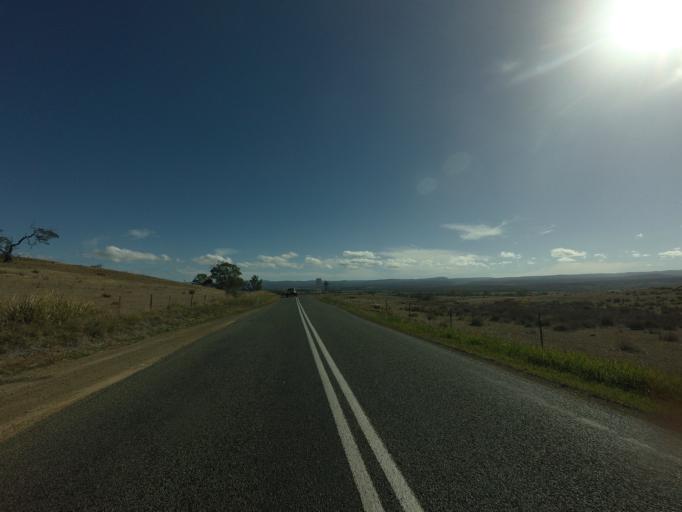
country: AU
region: Tasmania
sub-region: Break O'Day
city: St Helens
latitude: -41.9945
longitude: 148.0953
